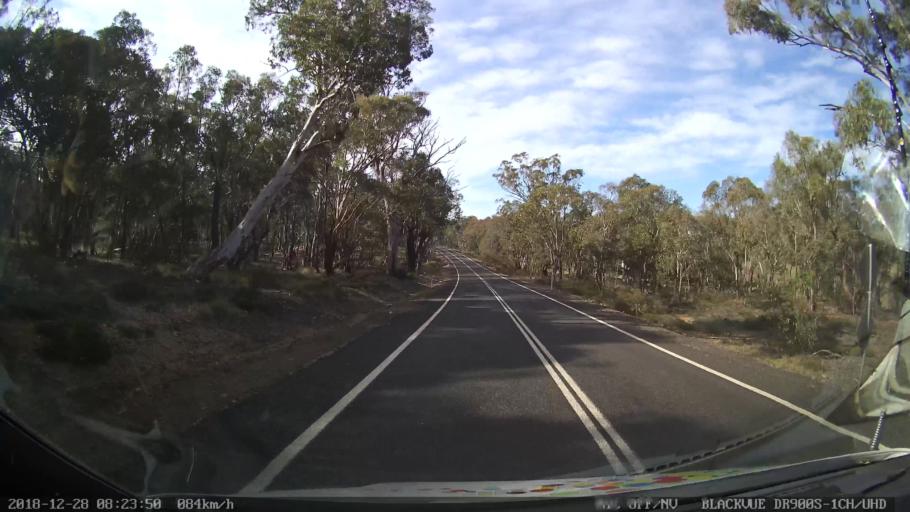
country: AU
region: New South Wales
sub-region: Blayney
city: Blayney
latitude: -33.9117
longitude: 149.3466
